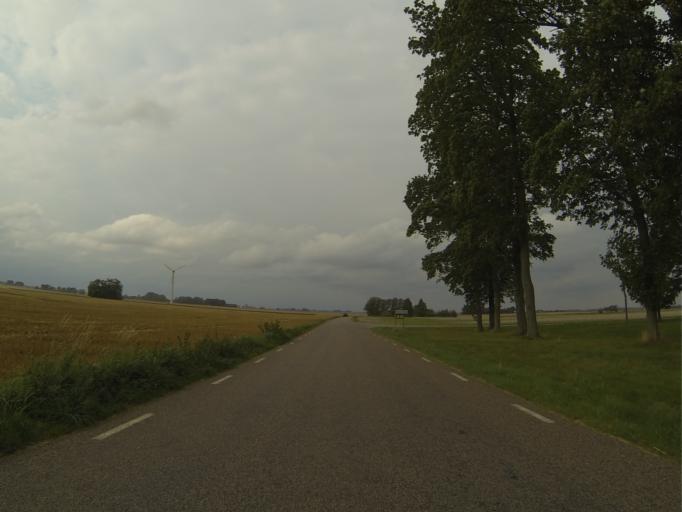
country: SE
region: Skane
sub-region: Lunds Kommun
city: Lund
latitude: 55.7801
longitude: 13.1894
